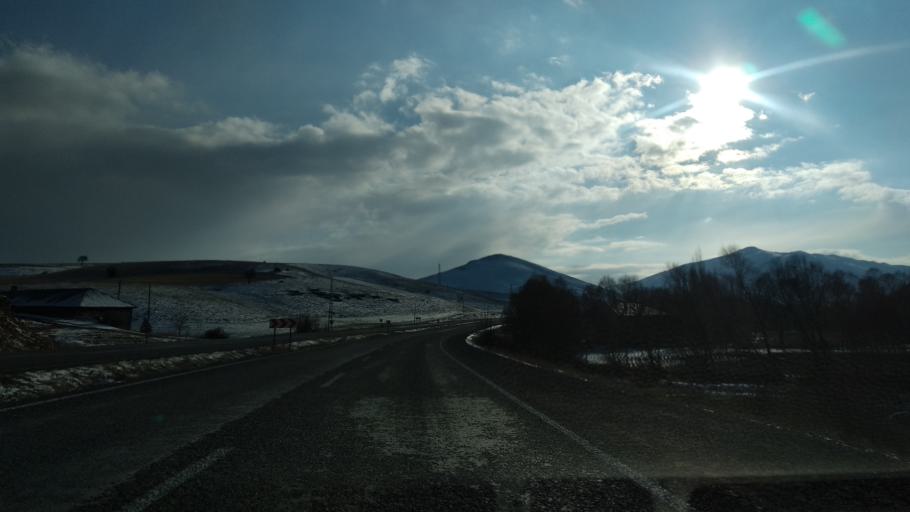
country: TR
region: Kayseri
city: Sariz
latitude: 38.3620
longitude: 36.4414
